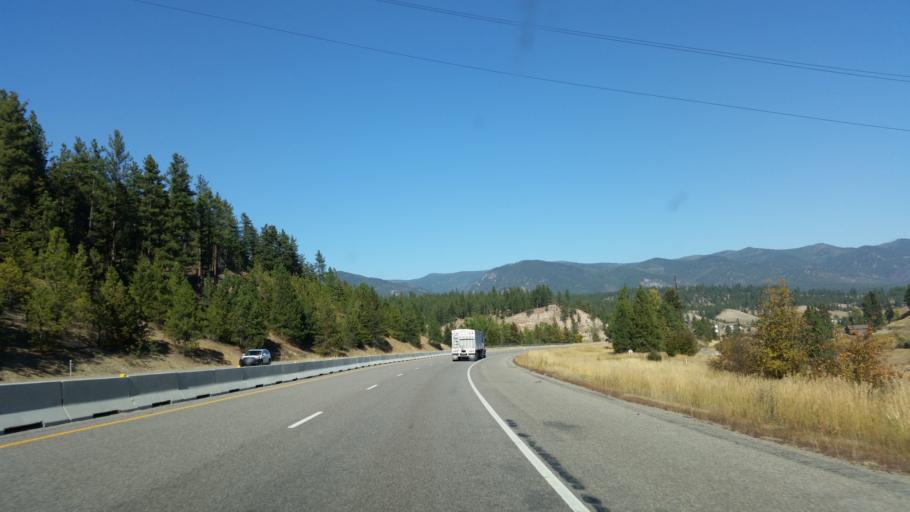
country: US
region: Montana
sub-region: Missoula County
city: Frenchtown
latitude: 47.0295
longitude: -114.3564
